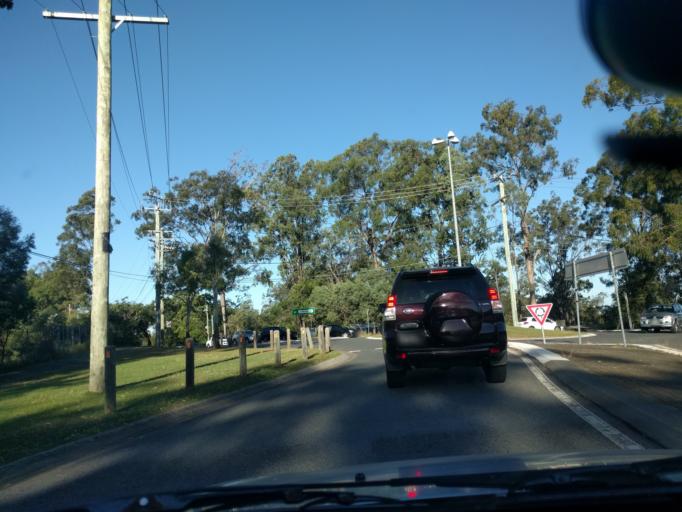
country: AU
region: Queensland
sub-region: Brisbane
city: Kenmore Hills
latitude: -27.5102
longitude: 152.9557
